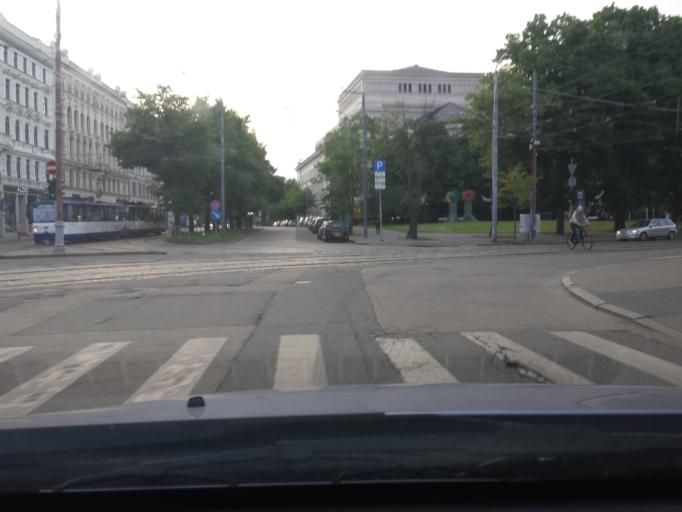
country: LV
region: Riga
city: Riga
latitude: 56.9478
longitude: 24.1148
